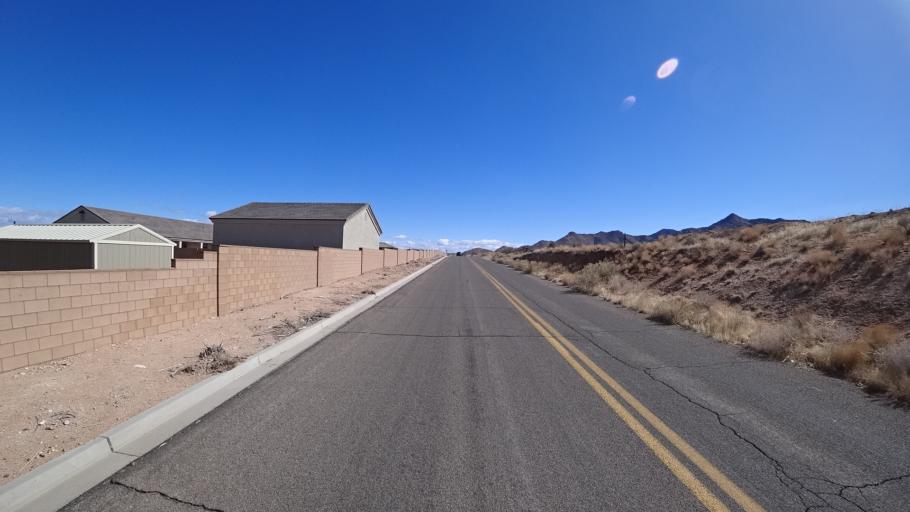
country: US
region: Arizona
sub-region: Mohave County
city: Kingman
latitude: 35.1959
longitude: -113.9675
